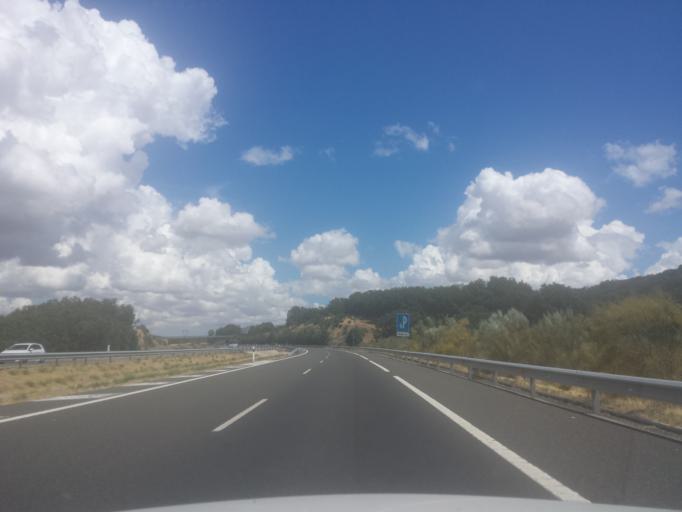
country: ES
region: Castille and Leon
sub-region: Provincia de Salamanca
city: Cantagallo
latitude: 40.3692
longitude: -5.8279
